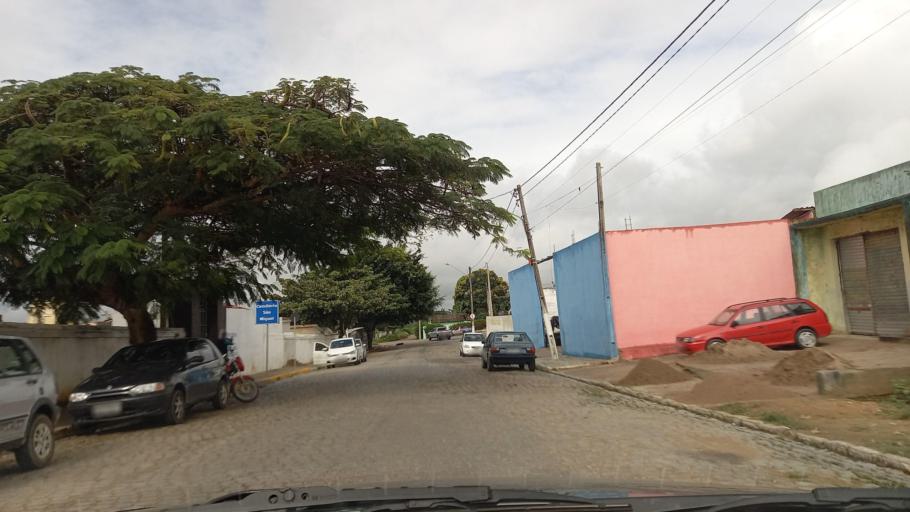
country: BR
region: Pernambuco
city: Garanhuns
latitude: -8.9058
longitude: -36.4974
